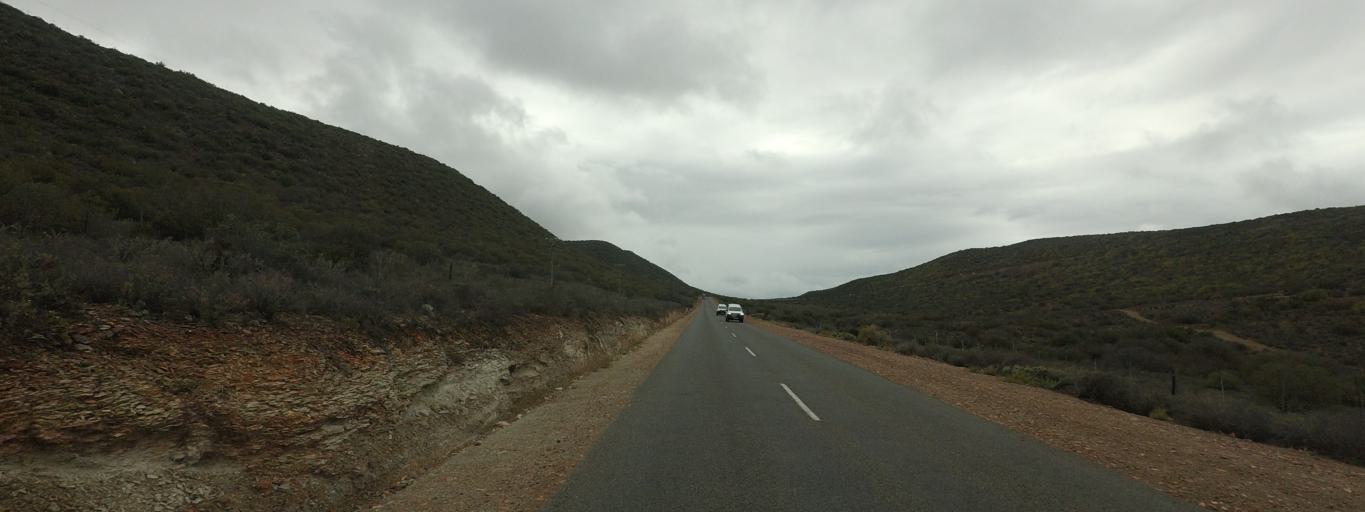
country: ZA
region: Western Cape
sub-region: Eden District Municipality
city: Oudtshoorn
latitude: -33.6845
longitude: 22.2635
